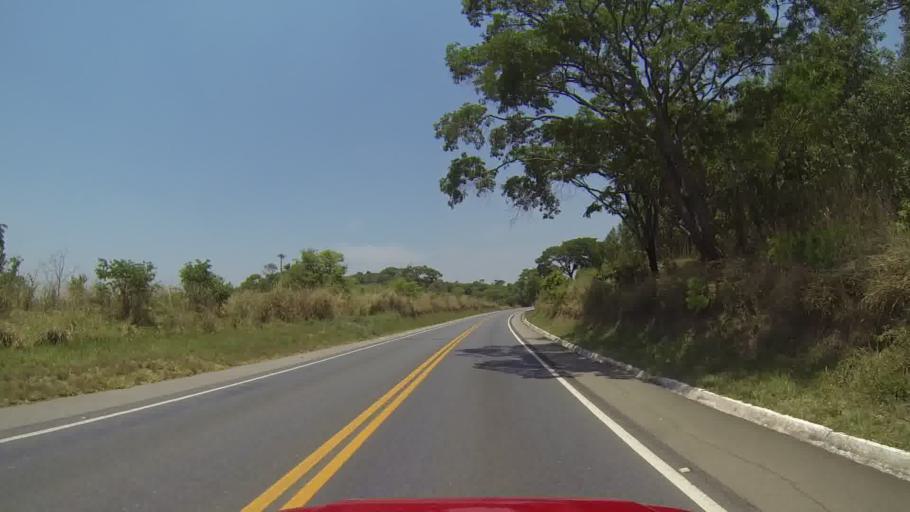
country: BR
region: Minas Gerais
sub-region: Itapecerica
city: Itapecerica
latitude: -20.3177
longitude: -45.2205
